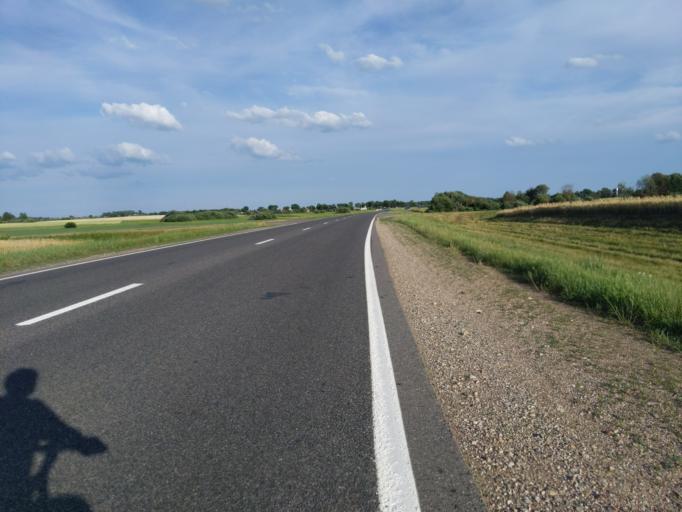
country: BY
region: Minsk
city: Nyasvizh
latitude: 53.2367
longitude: 26.7161
